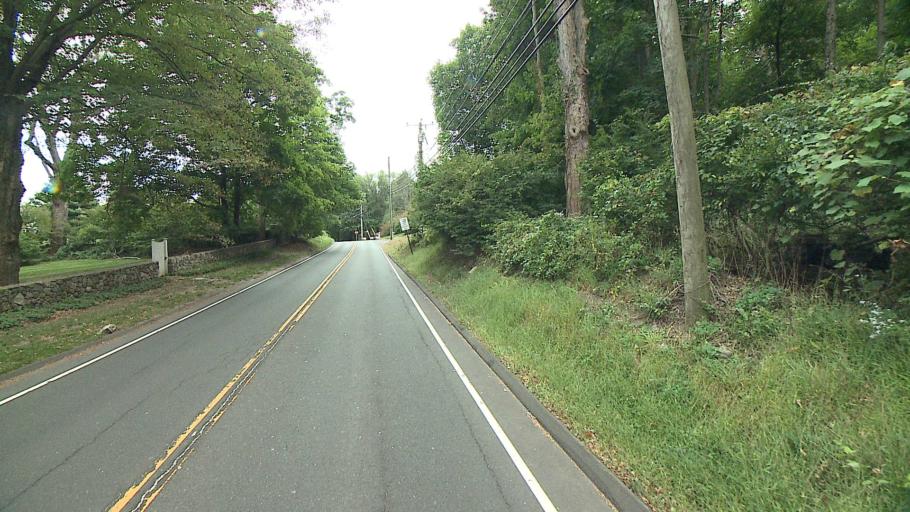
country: US
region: Connecticut
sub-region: Fairfield County
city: Wilton
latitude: 41.2043
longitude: -73.4534
